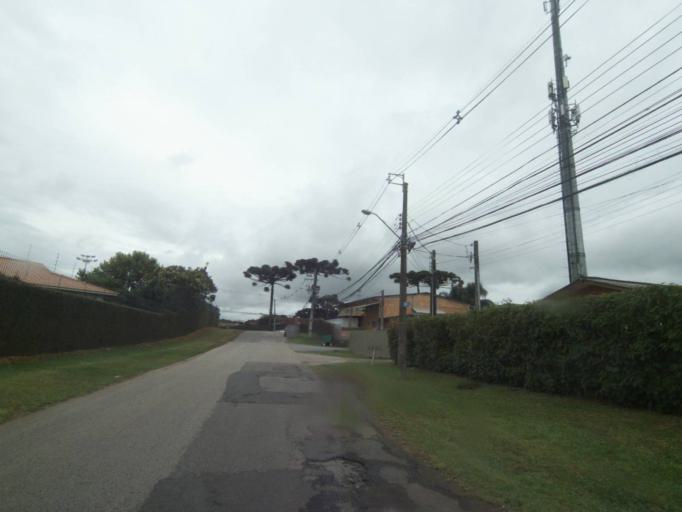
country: BR
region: Parana
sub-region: Curitiba
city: Curitiba
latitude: -25.4576
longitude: -49.3345
